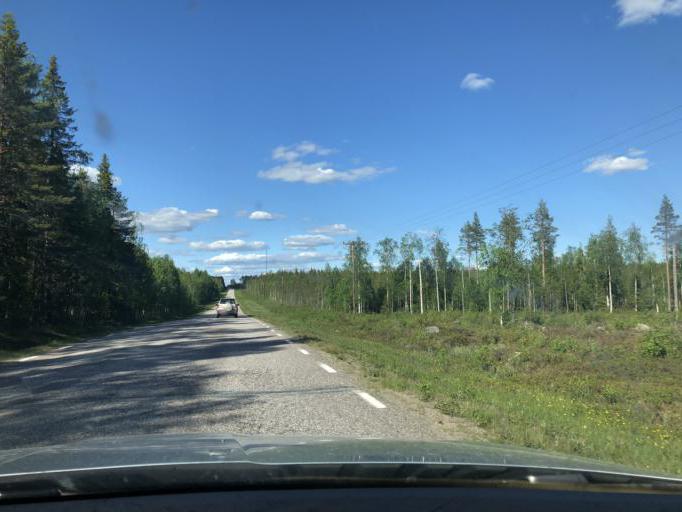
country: SE
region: Norrbotten
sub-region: Kalix Kommun
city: Kalix
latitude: 66.0307
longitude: 23.1682
